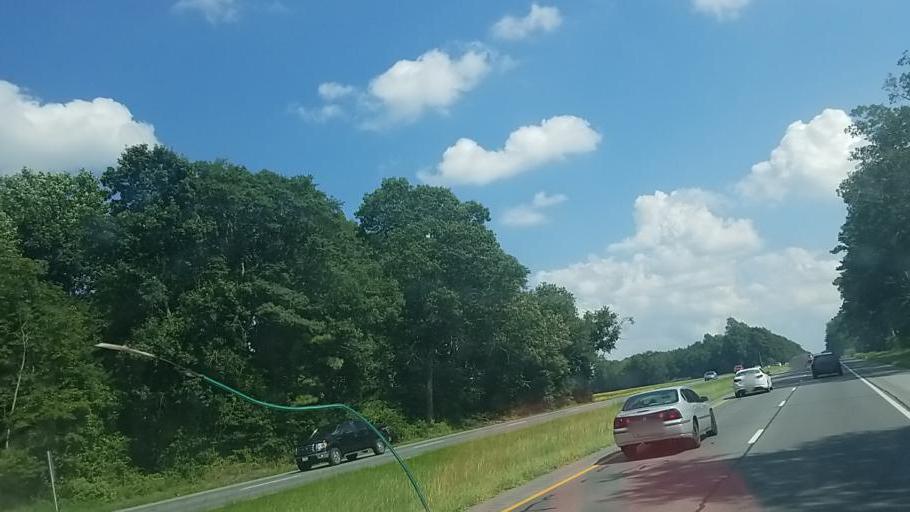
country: US
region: Delaware
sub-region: Sussex County
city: Millsboro
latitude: 38.6135
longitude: -75.3311
